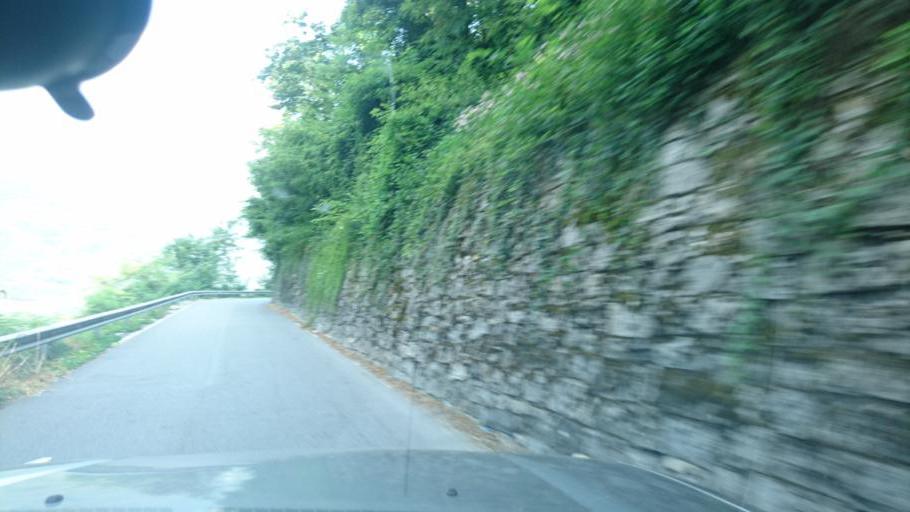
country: IT
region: Lombardy
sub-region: Provincia di Brescia
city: Breno
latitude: 45.9513
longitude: 10.3047
